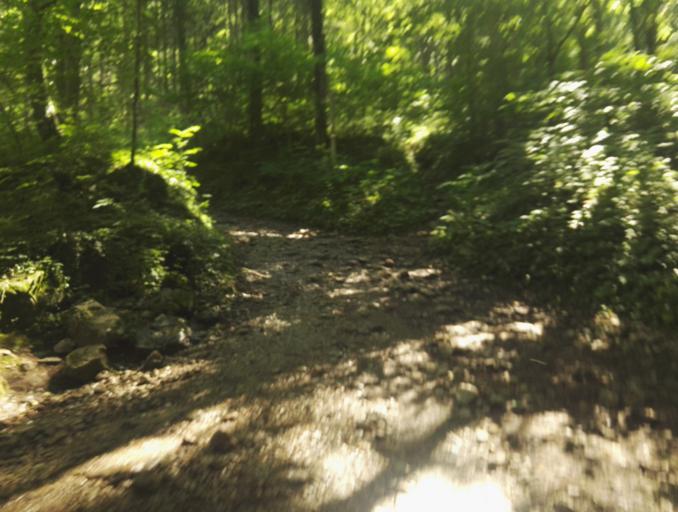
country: AT
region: Styria
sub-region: Politischer Bezirk Graz-Umgebung
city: Rothelstein
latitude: 47.3378
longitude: 15.3846
